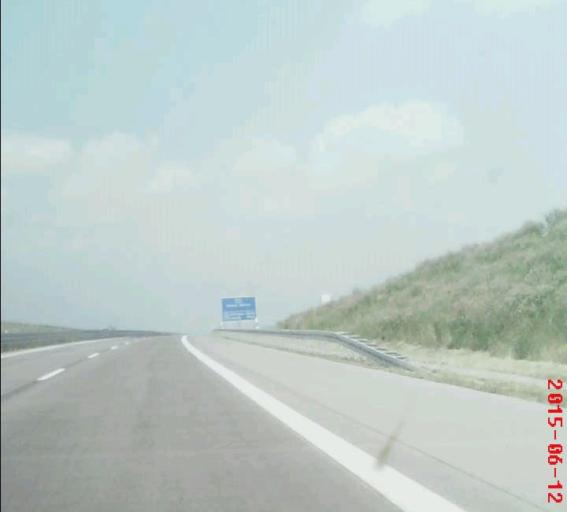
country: DE
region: Thuringia
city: Artern
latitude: 51.3850
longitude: 11.2785
